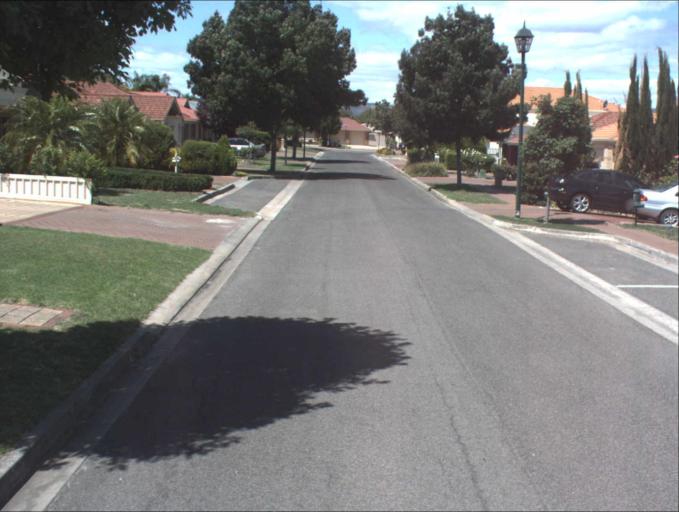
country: AU
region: South Australia
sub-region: Port Adelaide Enfield
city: Gilles Plains
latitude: -34.8518
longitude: 138.6454
